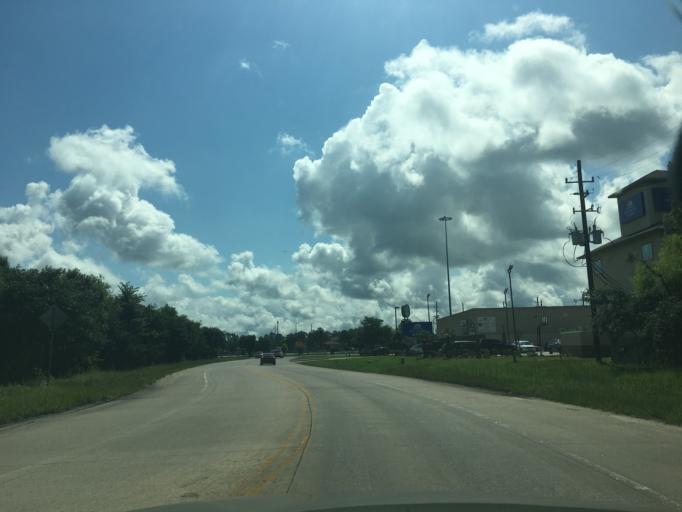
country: US
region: Texas
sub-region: Harris County
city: Spring
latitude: 30.0652
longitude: -95.4367
